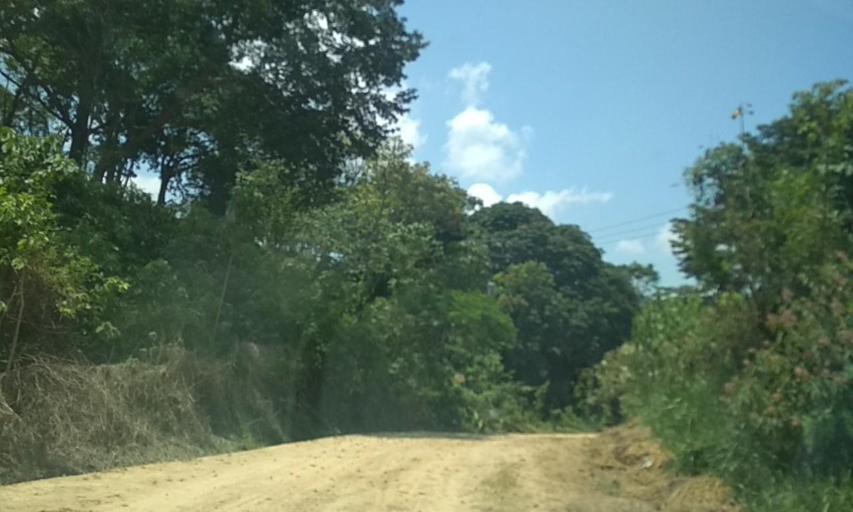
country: MX
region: Chiapas
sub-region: Tecpatan
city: Raudales Malpaso
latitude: 17.3933
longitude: -93.7288
